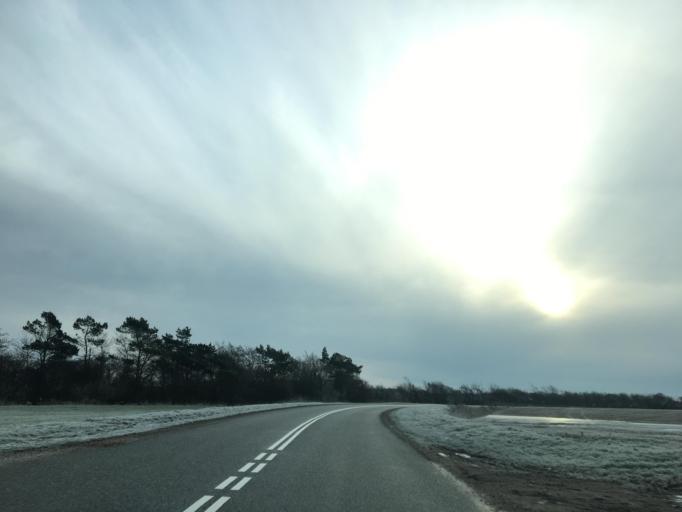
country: DK
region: North Denmark
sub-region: Thisted Kommune
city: Hurup
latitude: 56.7580
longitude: 8.4190
